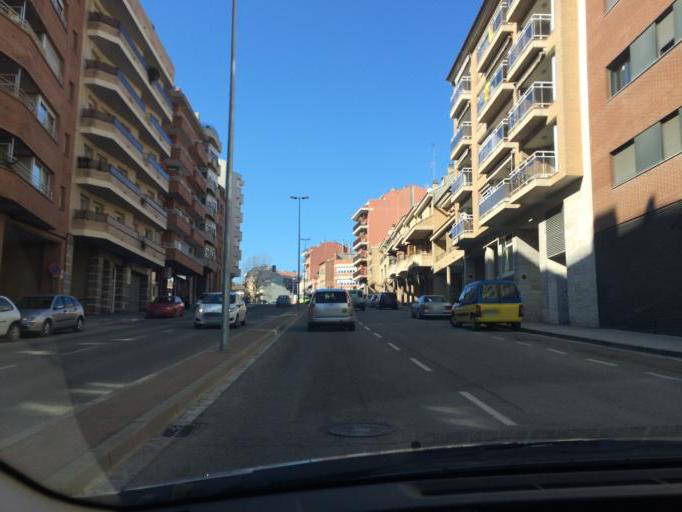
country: ES
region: Catalonia
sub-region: Provincia de Barcelona
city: Manresa
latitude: 41.7354
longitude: 1.8346
